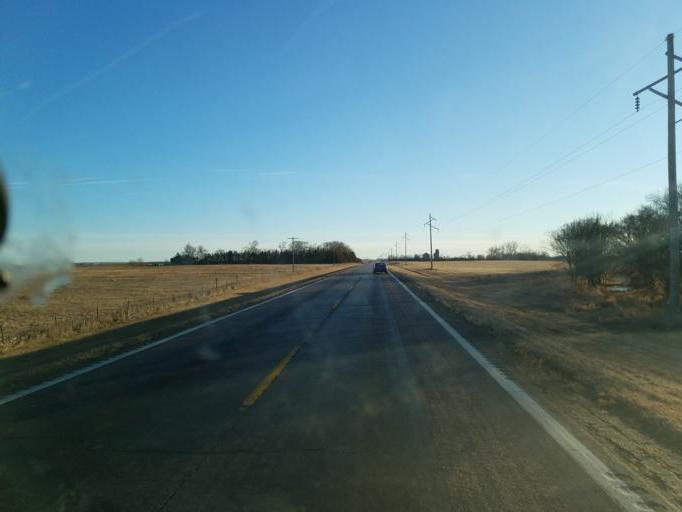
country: US
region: South Dakota
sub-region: Bon Homme County
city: Tyndall
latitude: 42.9505
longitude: -97.8919
